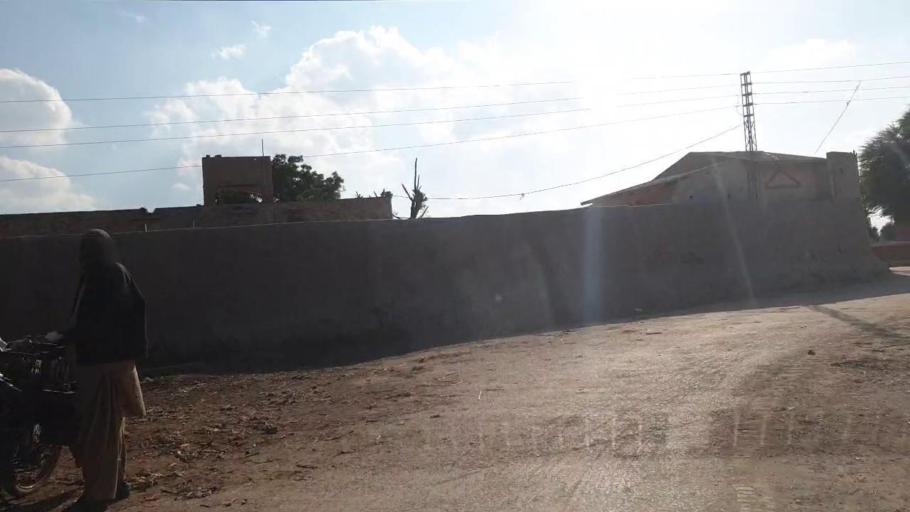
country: PK
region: Sindh
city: Shahpur Chakar
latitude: 26.1002
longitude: 68.5926
